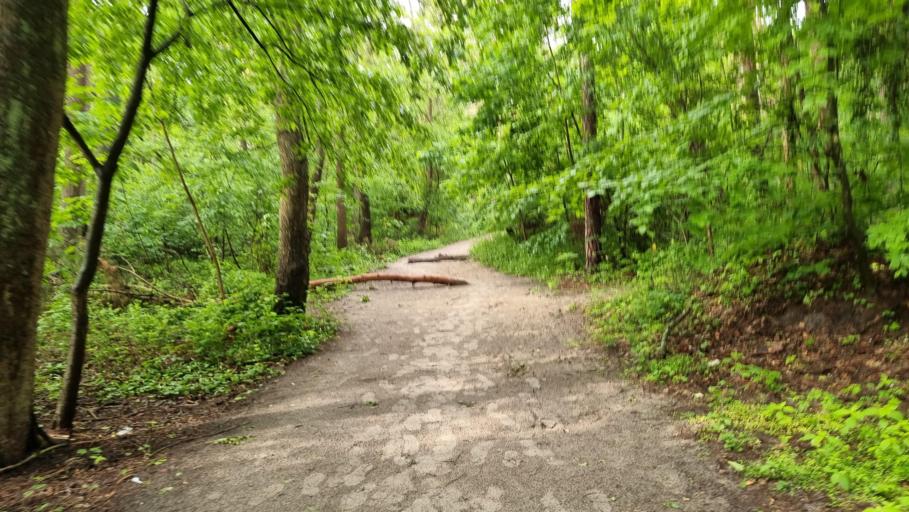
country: PL
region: West Pomeranian Voivodeship
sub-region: Swinoujscie
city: Swinoujscie
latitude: 53.9203
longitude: 14.2374
